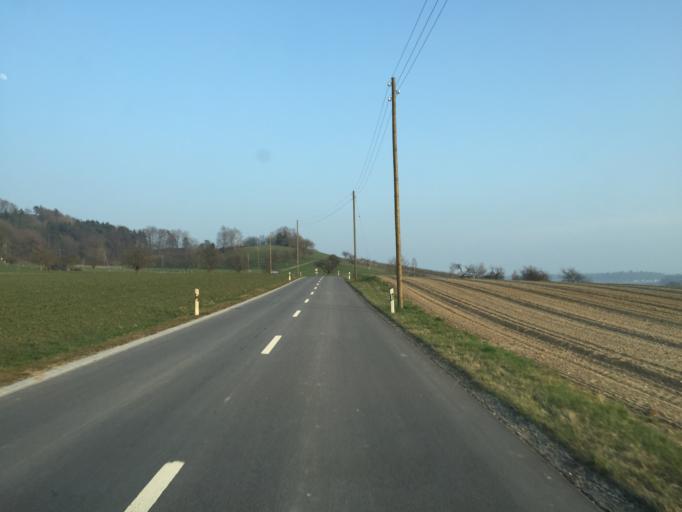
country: CH
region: Zurich
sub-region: Bezirk Andelfingen
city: Uhwiesen
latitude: 47.6597
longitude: 8.6417
